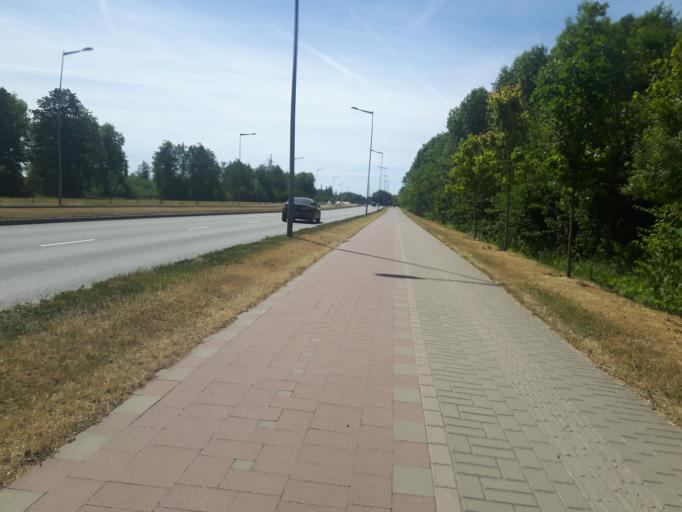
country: LV
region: Liepaja
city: Vec-Liepaja
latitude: 56.5341
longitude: 21.0521
